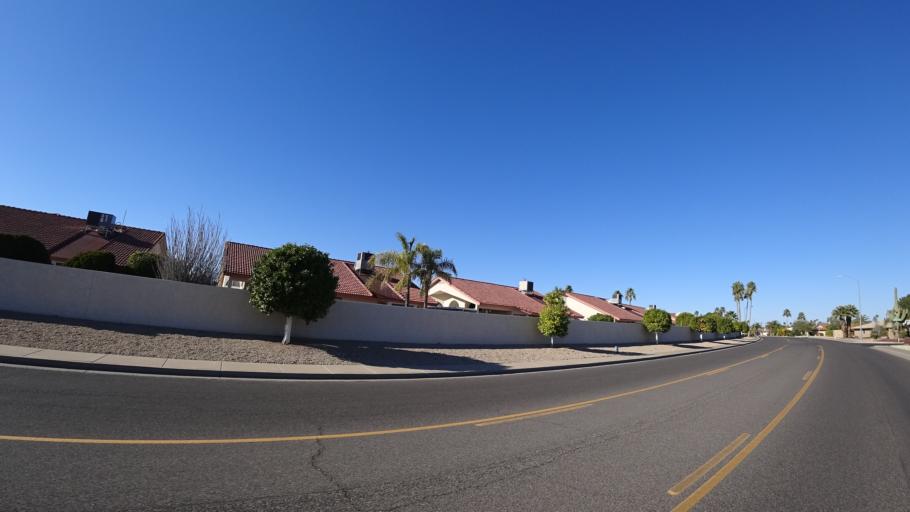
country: US
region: Arizona
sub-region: Maricopa County
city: Sun City West
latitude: 33.6635
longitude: -112.3408
